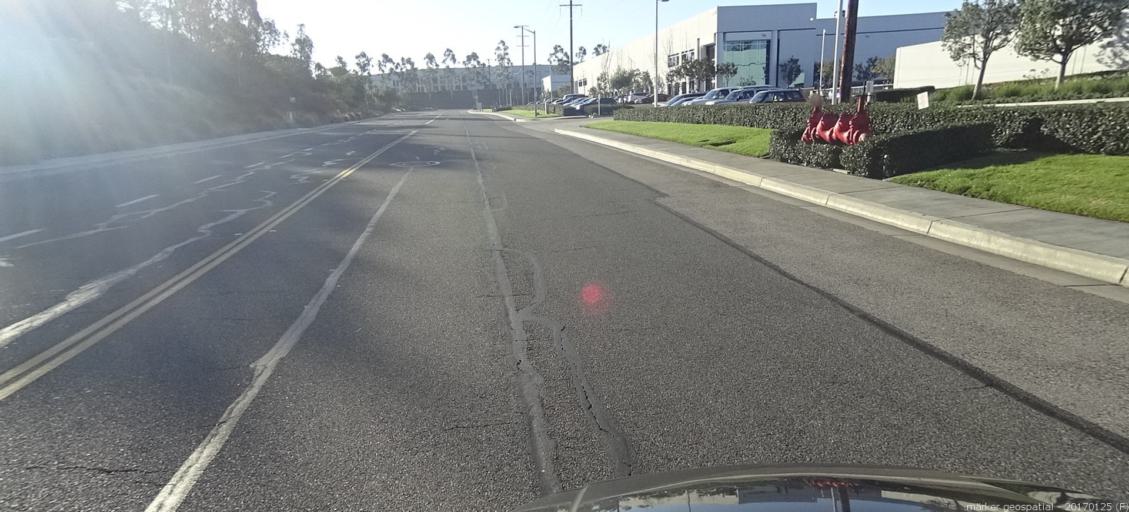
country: US
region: California
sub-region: Orange County
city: Foothill Ranch
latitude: 33.6718
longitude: -117.6490
